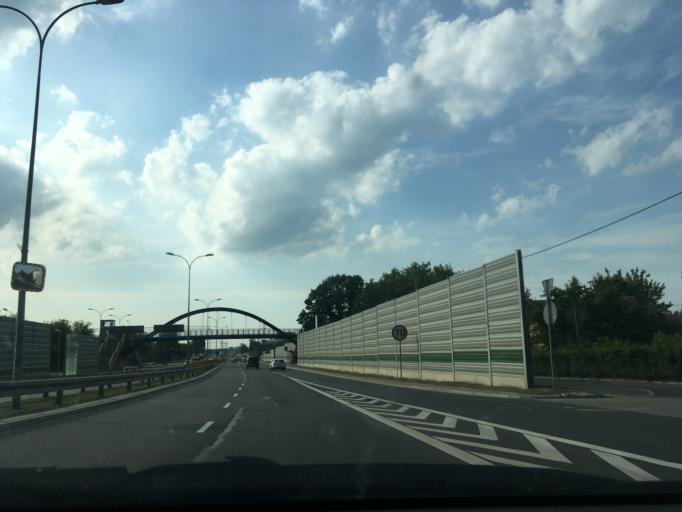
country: PL
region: Podlasie
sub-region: Bialystok
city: Bialystok
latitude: 53.1473
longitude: 23.1795
